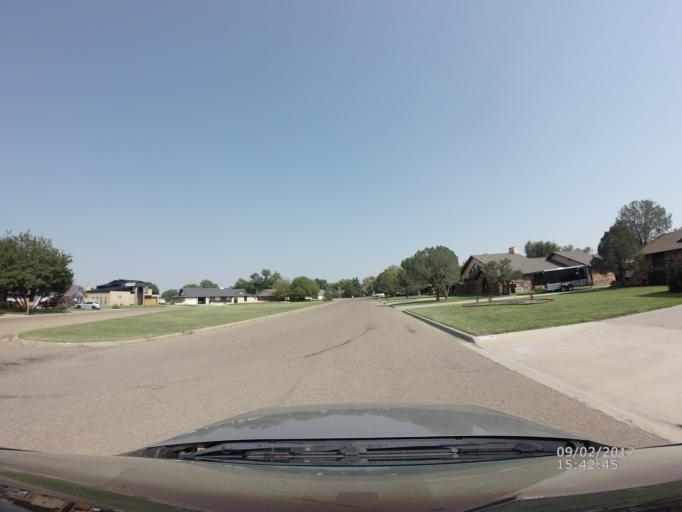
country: US
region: New Mexico
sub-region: Curry County
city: Clovis
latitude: 34.4438
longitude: -103.1915
